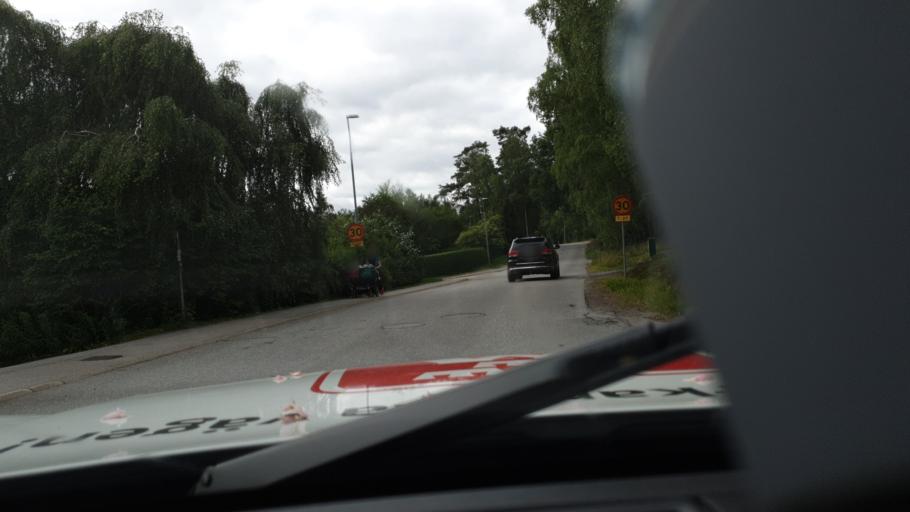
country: SE
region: Stockholm
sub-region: Vallentuna Kommun
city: Vallentuna
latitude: 59.5142
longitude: 18.0630
